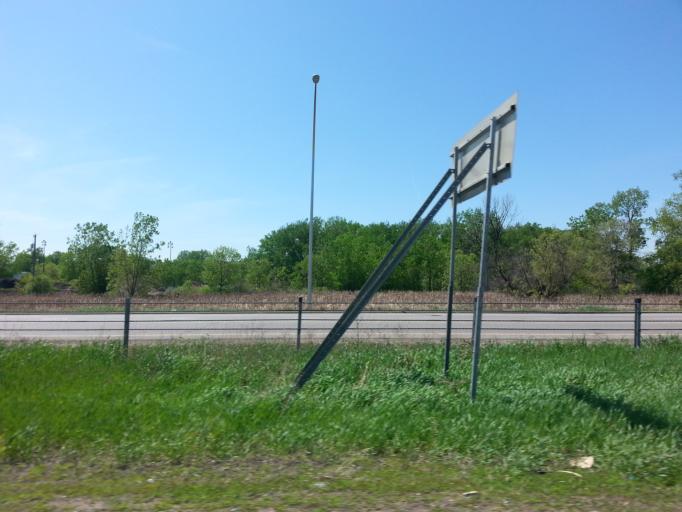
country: US
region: Minnesota
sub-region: Hennepin County
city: Richfield
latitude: 44.8912
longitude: -93.2469
